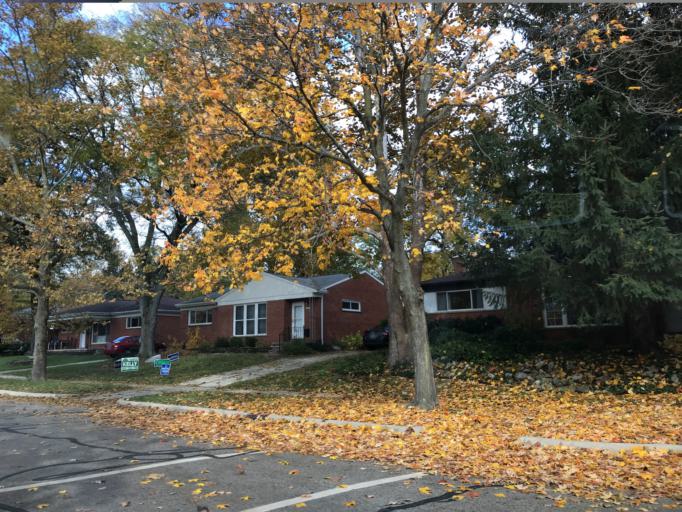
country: US
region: Michigan
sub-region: Washtenaw County
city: Ann Arbor
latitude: 42.2547
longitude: -83.7124
